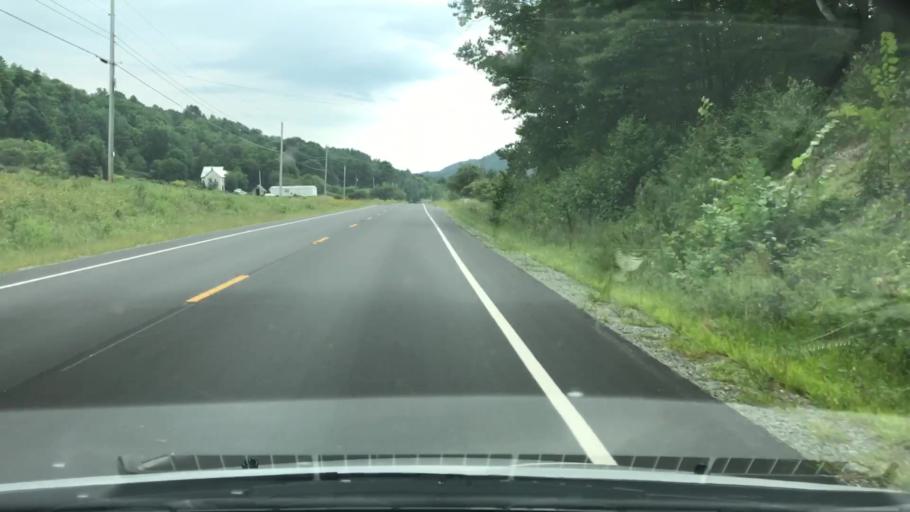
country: US
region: New Hampshire
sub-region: Grafton County
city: Orford
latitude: 43.8633
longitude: -72.1551
